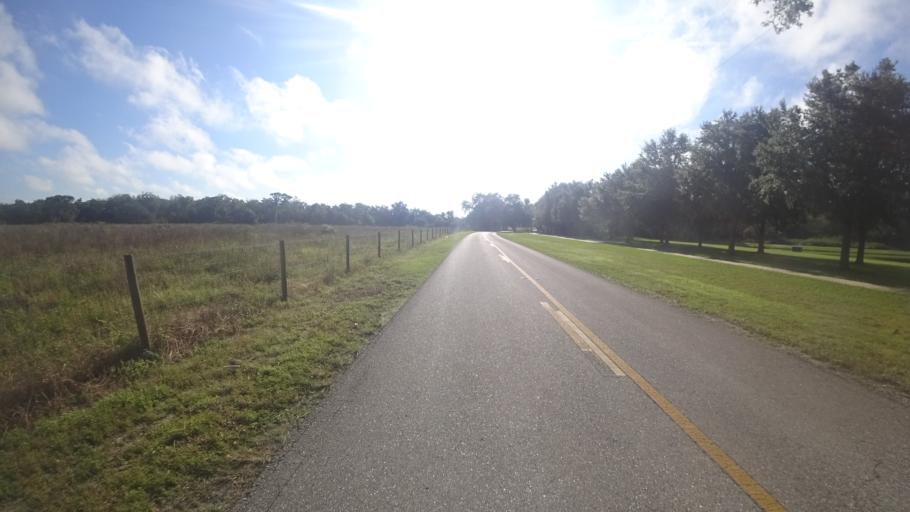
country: US
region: Florida
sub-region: Manatee County
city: Ellenton
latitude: 27.5636
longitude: -82.4068
